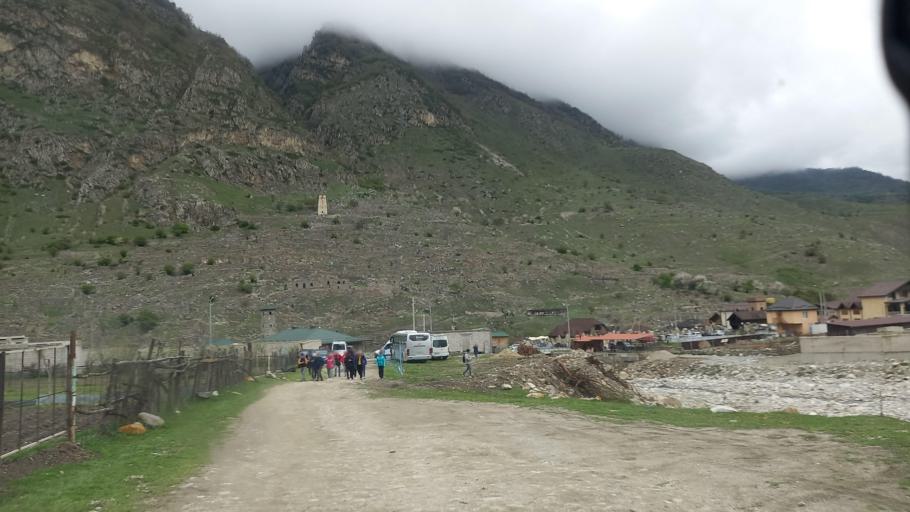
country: RU
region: Kabardino-Balkariya
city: Verkhnyaya Balkariya
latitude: 43.1038
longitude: 43.4339
